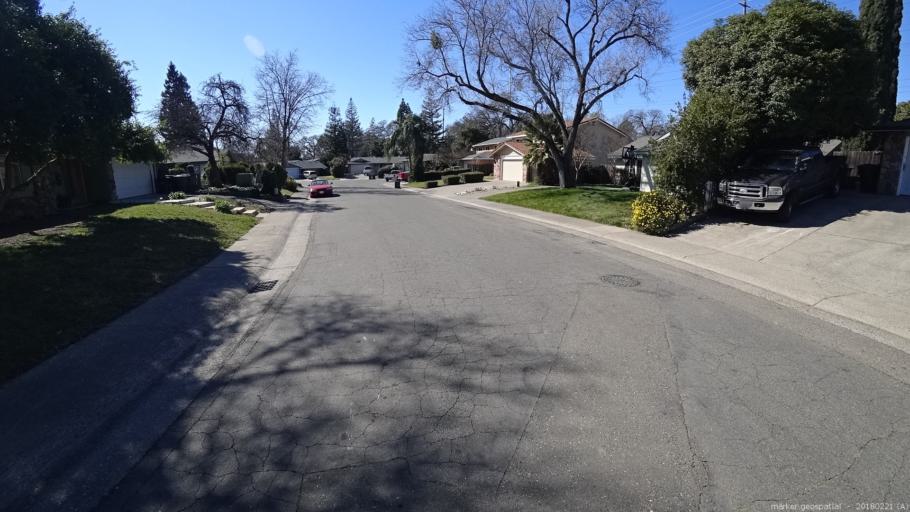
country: US
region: California
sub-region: Sacramento County
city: Citrus Heights
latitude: 38.6910
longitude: -121.2555
